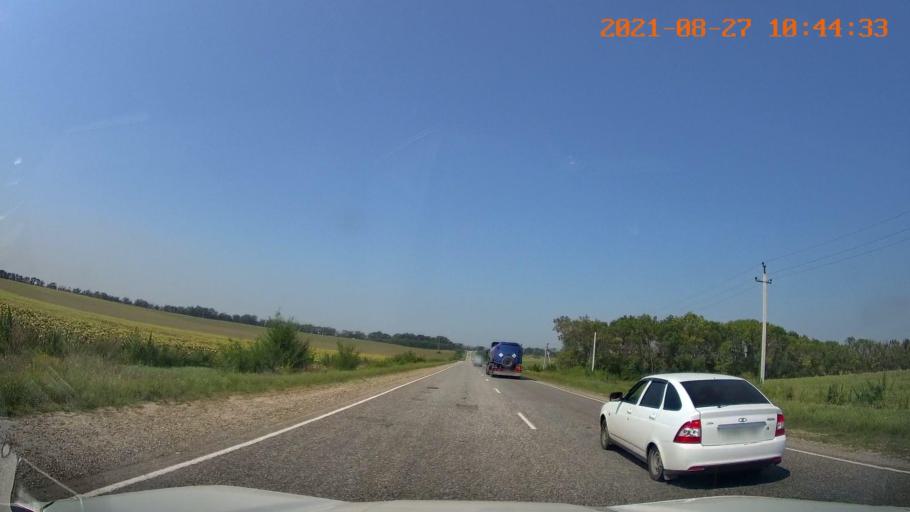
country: RU
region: Karachayevo-Cherkesiya
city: Psyzh
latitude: 44.3009
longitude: 42.0136
